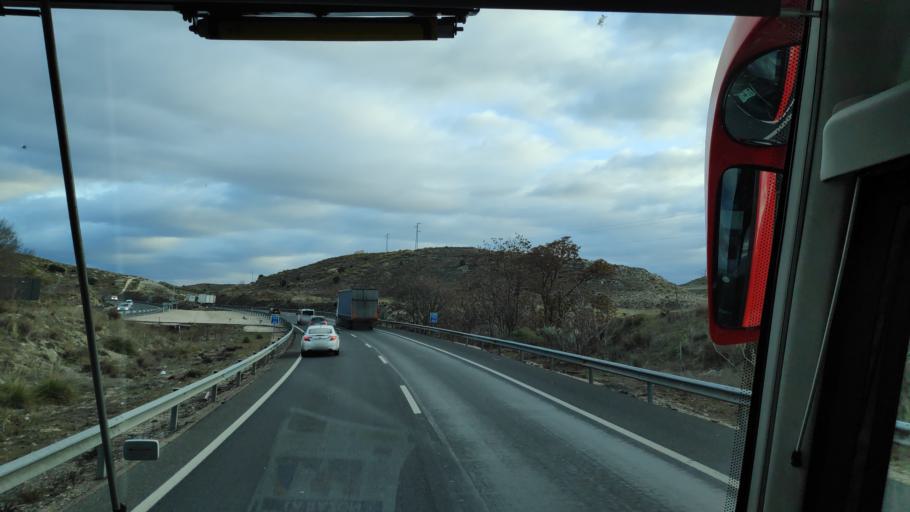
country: ES
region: Madrid
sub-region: Provincia de Madrid
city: Perales de Tajuna
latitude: 40.2154
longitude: -3.3292
